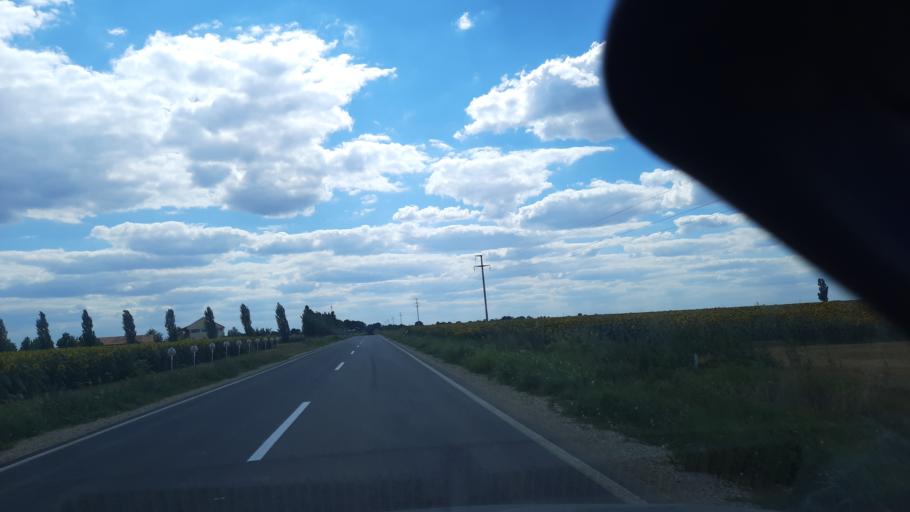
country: RS
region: Autonomna Pokrajina Vojvodina
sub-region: Sremski Okrug
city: Pecinci
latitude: 44.9222
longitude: 19.9833
